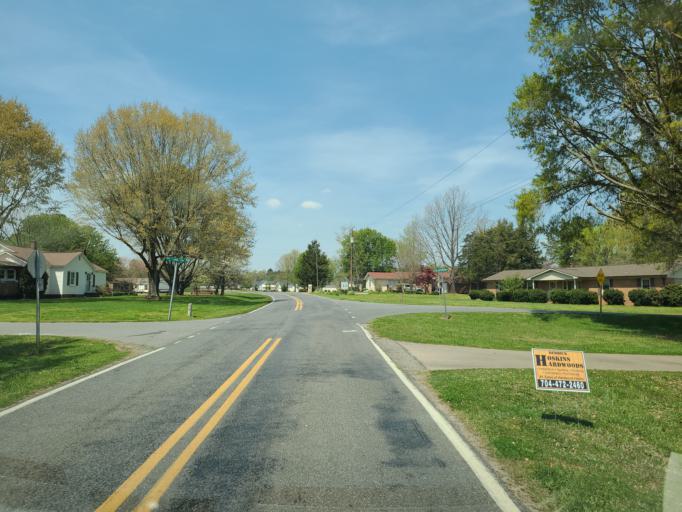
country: US
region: North Carolina
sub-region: Cleveland County
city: Shelby
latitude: 35.2607
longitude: -81.4953
